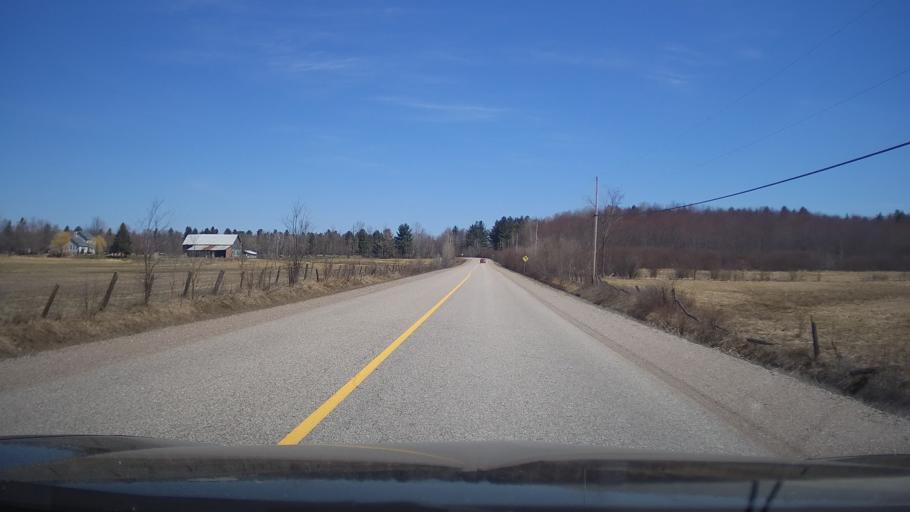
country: CA
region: Ontario
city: Arnprior
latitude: 45.5396
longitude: -76.3675
